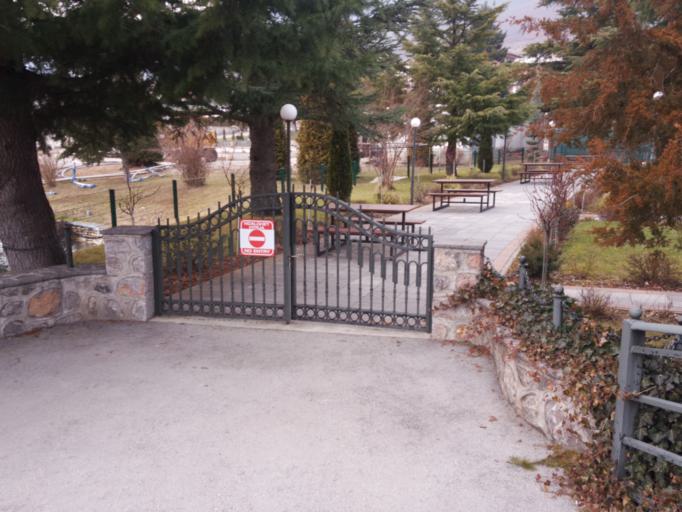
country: XK
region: Pec
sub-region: Komuna e Istogut
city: Istok
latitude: 42.7799
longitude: 20.4820
